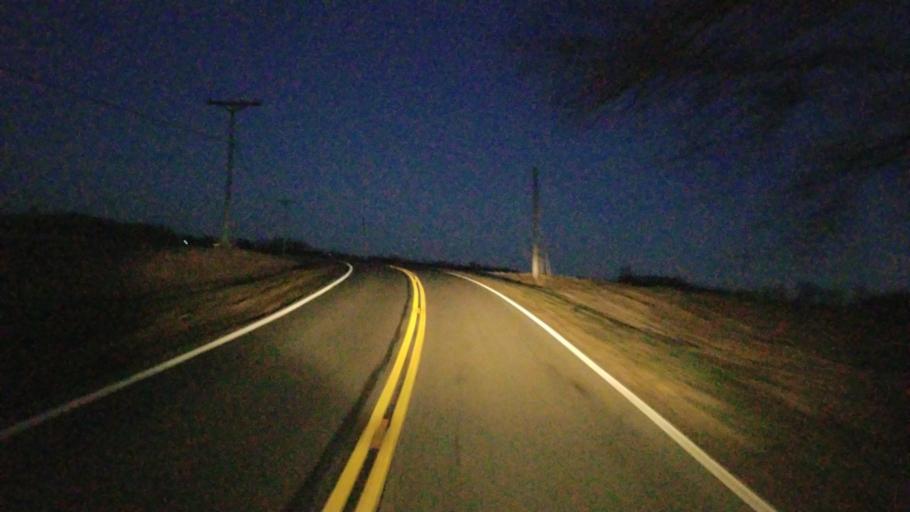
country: US
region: Ohio
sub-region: Highland County
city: Leesburg
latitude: 39.3022
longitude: -83.5188
